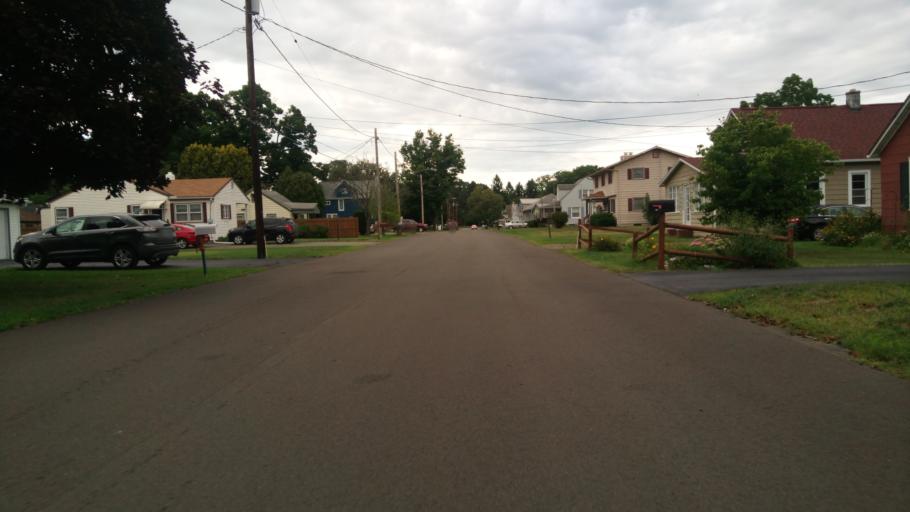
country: US
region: New York
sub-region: Chemung County
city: Southport
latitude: 42.0627
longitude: -76.8146
